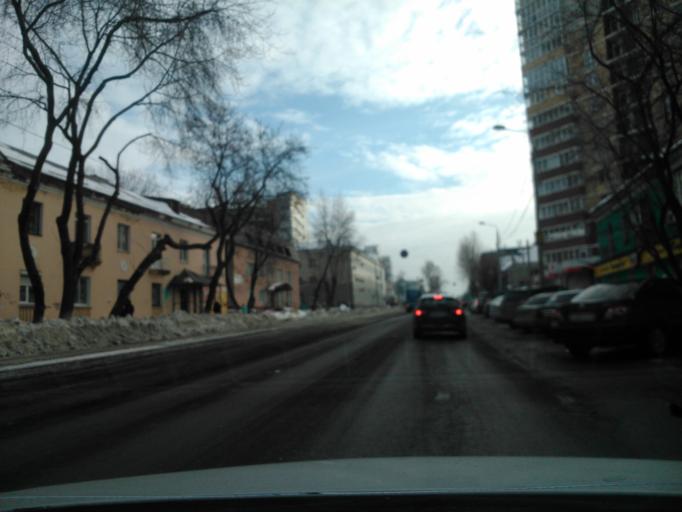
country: RU
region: Perm
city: Perm
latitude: 58.0000
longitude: 56.2409
